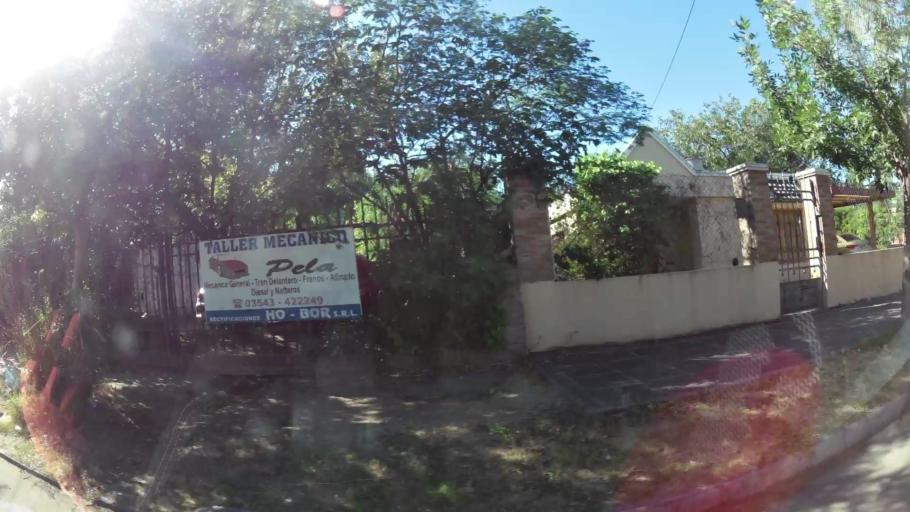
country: AR
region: Cordoba
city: Villa Allende
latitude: -31.3467
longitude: -64.2433
